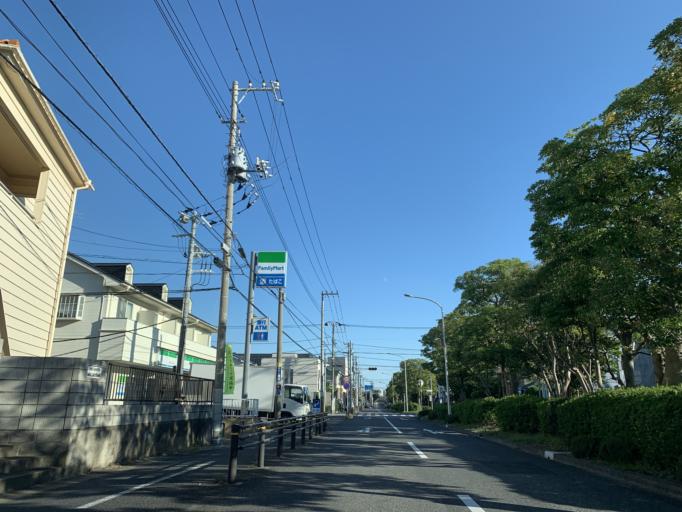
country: JP
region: Tokyo
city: Urayasu
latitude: 35.6569
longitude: 139.8916
